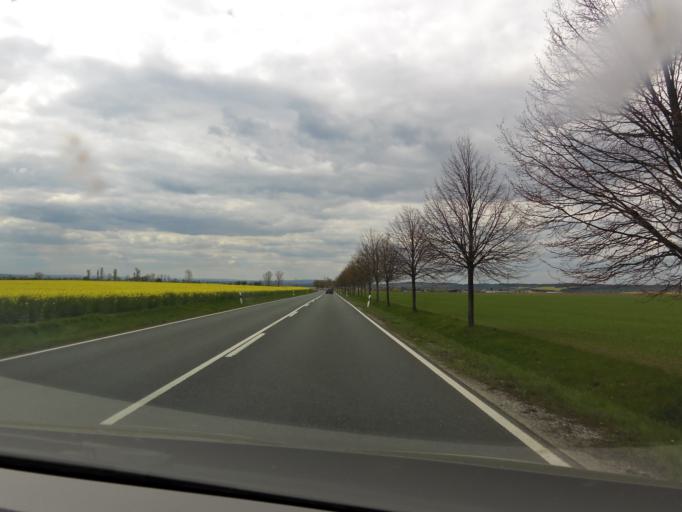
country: DE
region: Thuringia
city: Grossheringen
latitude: 51.1304
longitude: 11.6803
